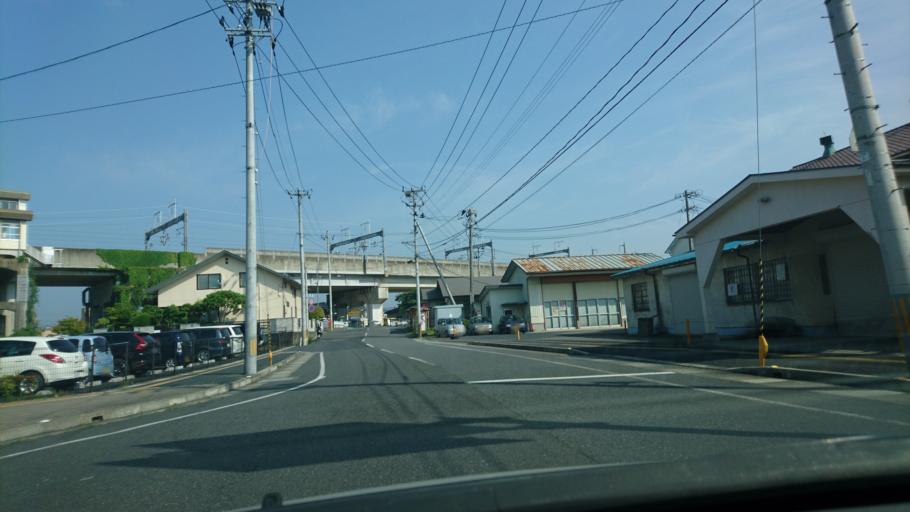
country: JP
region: Iwate
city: Ichinoseki
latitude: 38.9278
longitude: 141.1411
